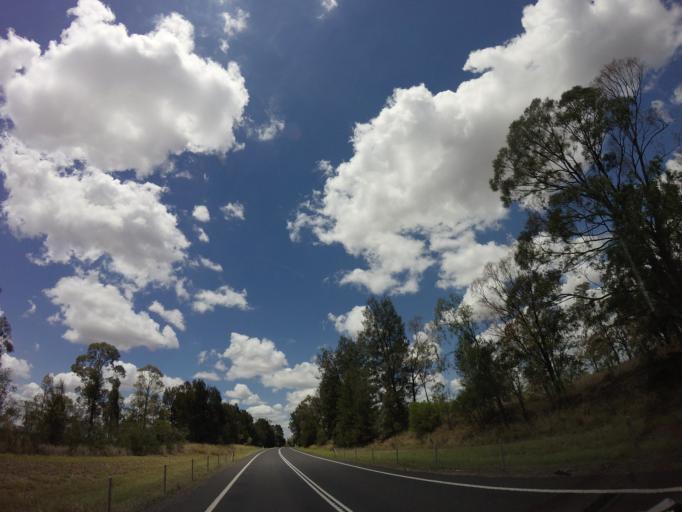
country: AU
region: Queensland
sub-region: Toowoomba
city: Oakey
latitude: -27.9061
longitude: 151.1907
